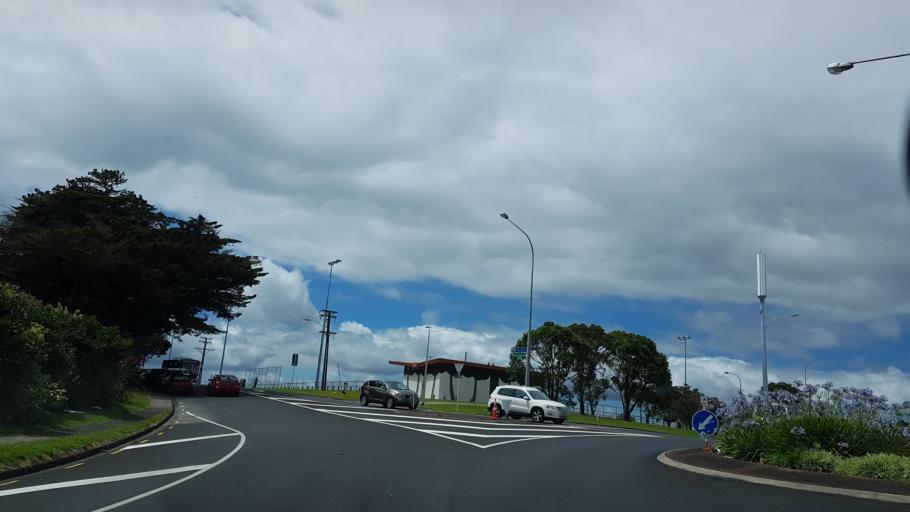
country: NZ
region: Auckland
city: Murrays Bay
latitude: -36.7562
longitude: 174.7511
